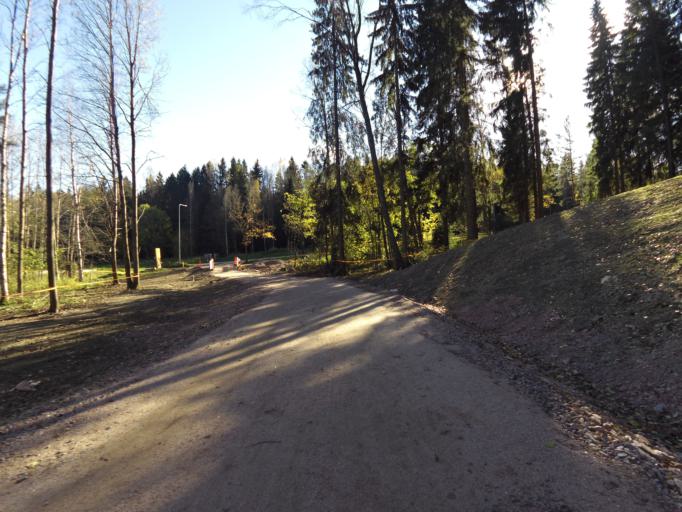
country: FI
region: Uusimaa
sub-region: Helsinki
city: Kauniainen
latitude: 60.1768
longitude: 24.7131
